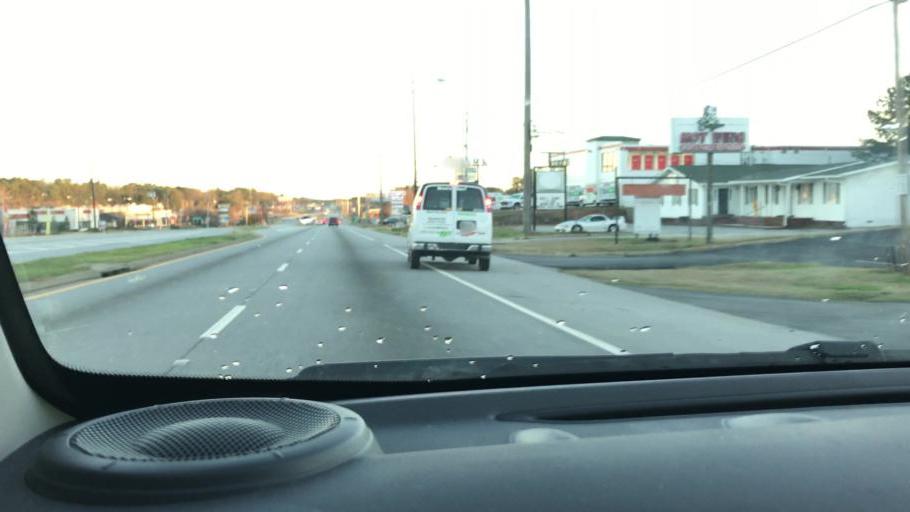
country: US
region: Georgia
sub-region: Clayton County
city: Riverdale
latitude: 33.5558
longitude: -84.4141
